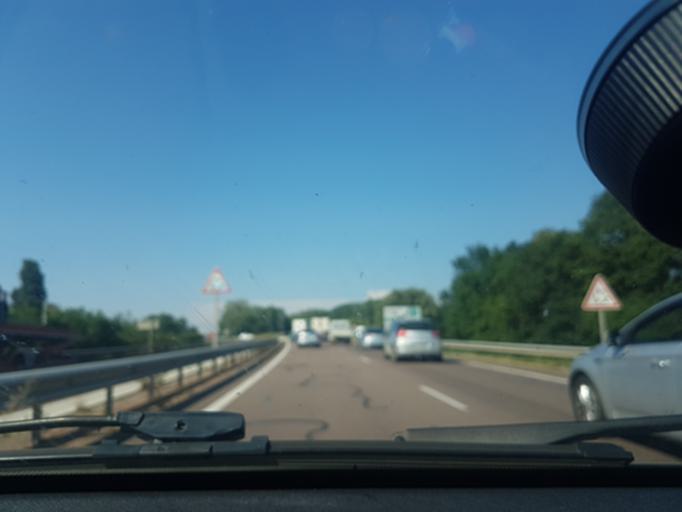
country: FR
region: Bourgogne
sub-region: Departement de Saone-et-Loire
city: Saint-Marcel
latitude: 46.7758
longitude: 4.8766
